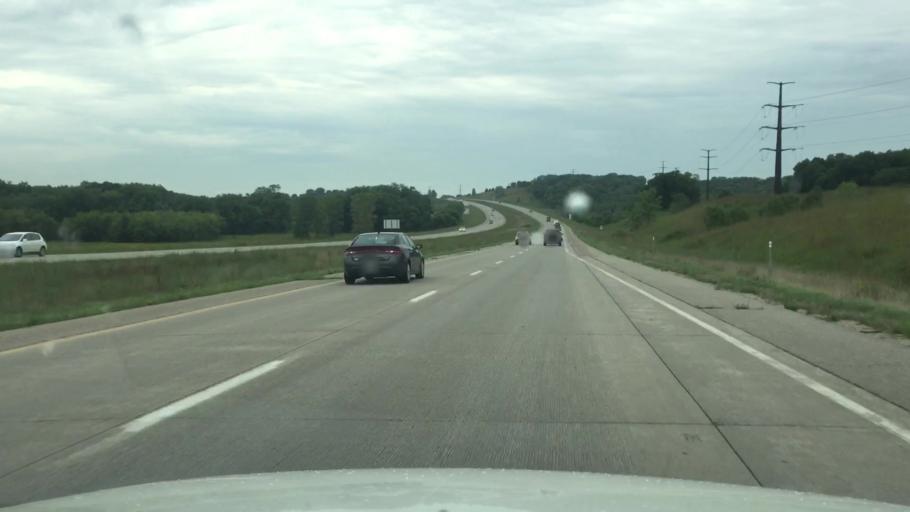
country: US
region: Iowa
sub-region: Warren County
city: Carlisle
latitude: 41.5047
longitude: -93.5825
